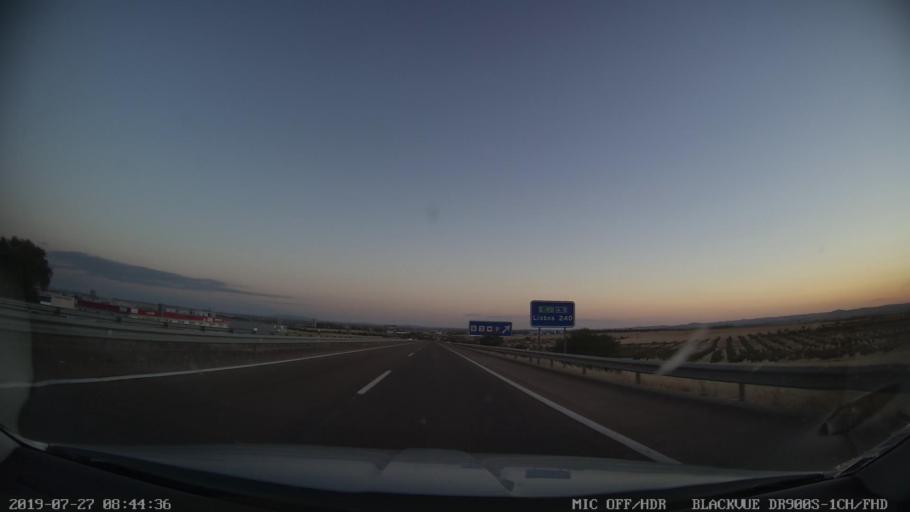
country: ES
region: Extremadura
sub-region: Provincia de Badajoz
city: Badajoz
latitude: 38.9007
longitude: -7.0012
